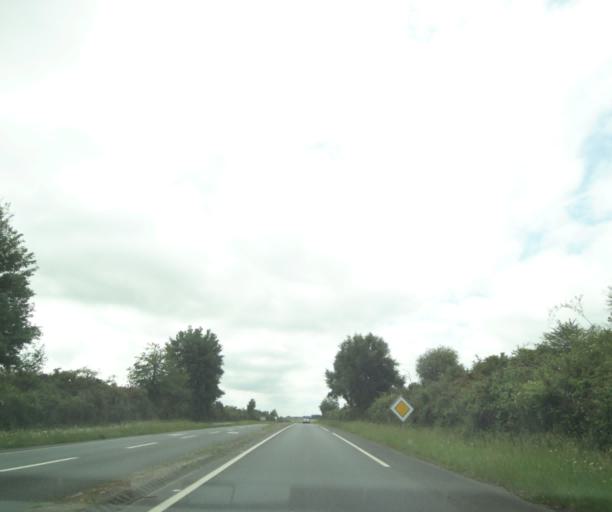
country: FR
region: Poitou-Charentes
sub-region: Departement des Deux-Sevres
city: Viennay
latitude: 46.7621
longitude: -0.2212
